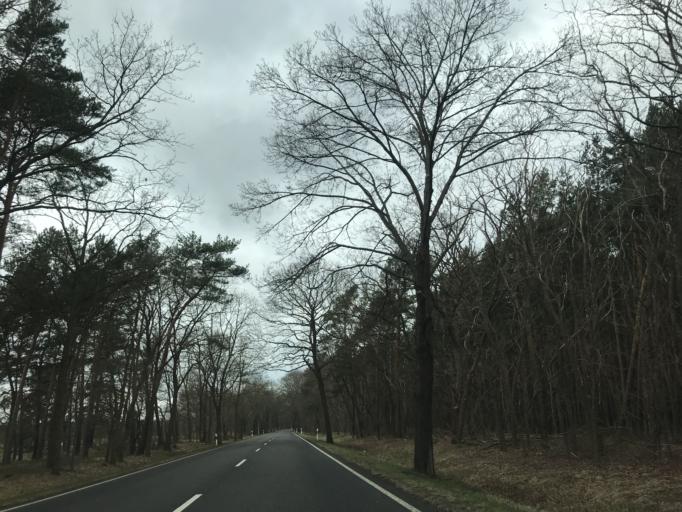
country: DE
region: Brandenburg
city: Kasel-Golzig
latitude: 51.9712
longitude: 13.6701
